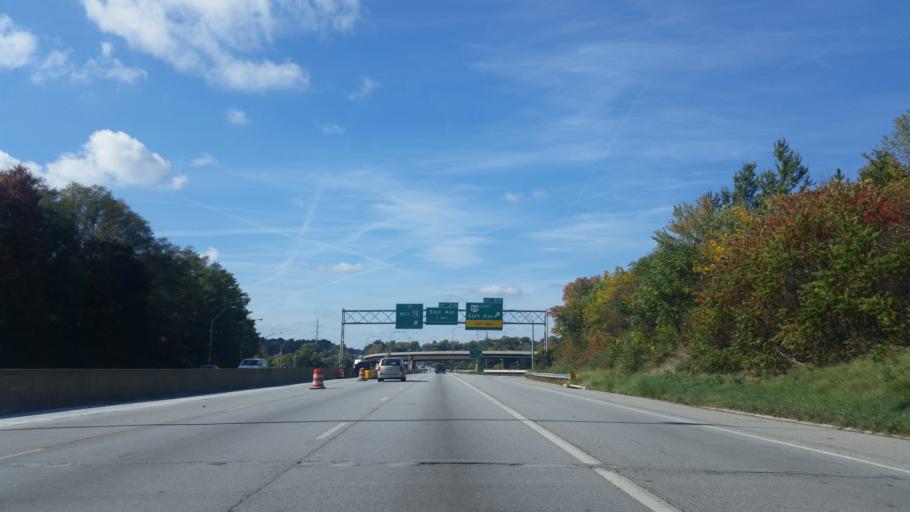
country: US
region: Ohio
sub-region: Summit County
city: Akron
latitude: 41.0622
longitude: -81.5350
